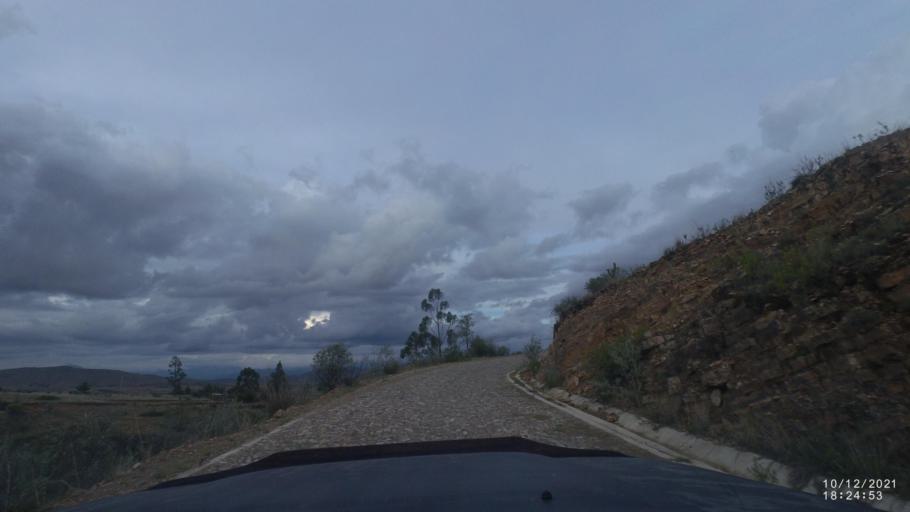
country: BO
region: Cochabamba
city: Tarata
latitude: -17.7893
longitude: -65.9739
